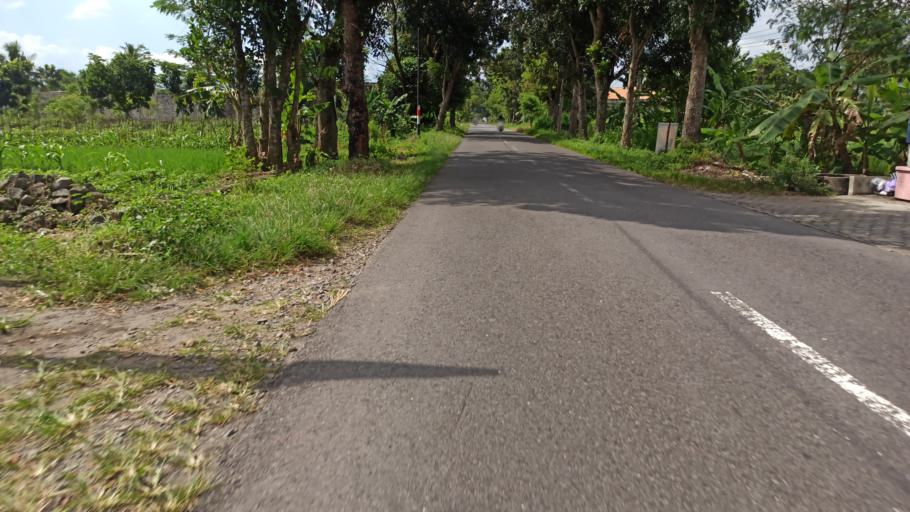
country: ID
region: Daerah Istimewa Yogyakarta
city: Sleman
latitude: -7.6901
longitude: 110.2962
